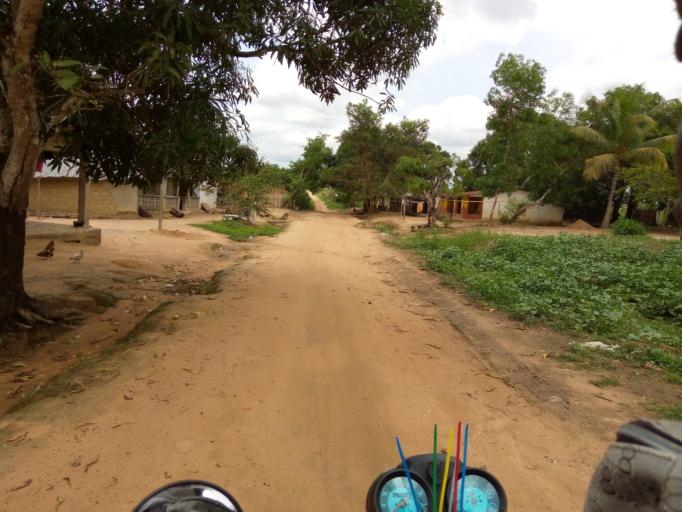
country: SL
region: Western Area
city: Waterloo
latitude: 8.3338
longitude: -12.9415
